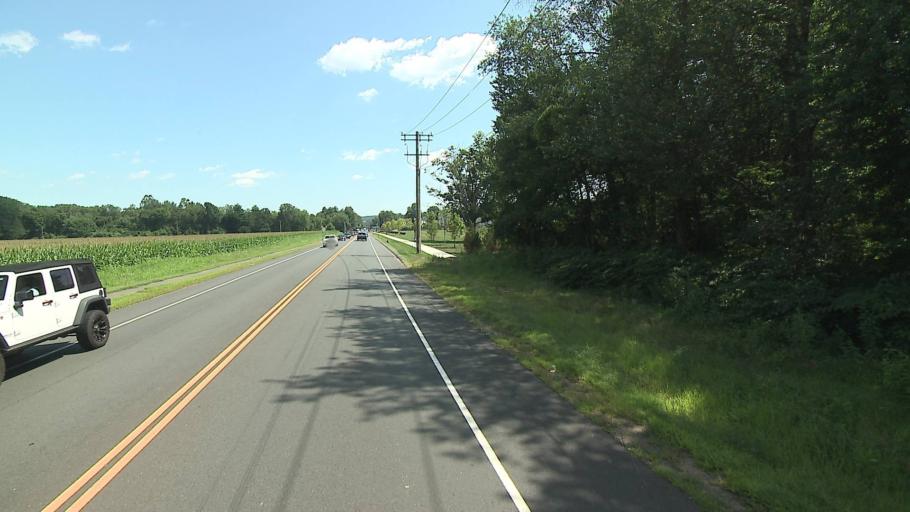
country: US
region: Connecticut
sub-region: Hartford County
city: Farmington
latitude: 41.7394
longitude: -72.8461
